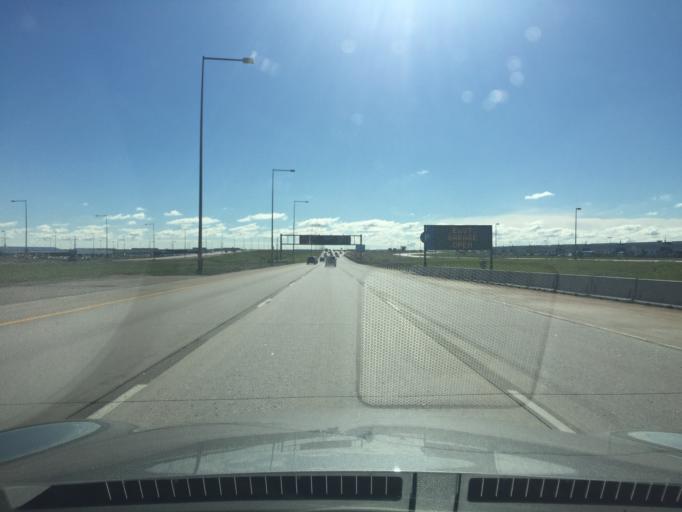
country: US
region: Colorado
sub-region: Adams County
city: Aurora
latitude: 39.8336
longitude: -104.7038
